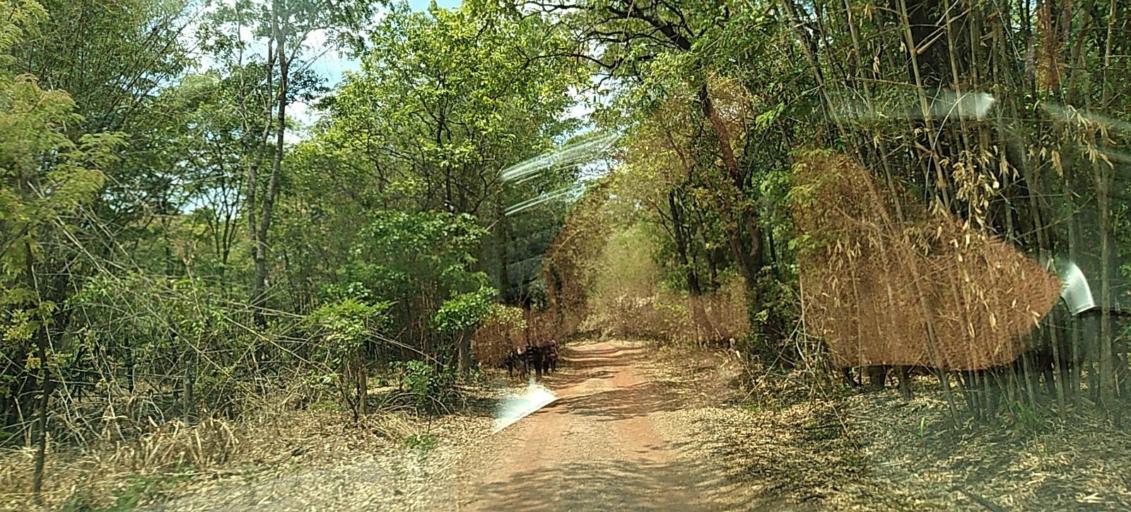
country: ZM
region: Copperbelt
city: Chililabombwe
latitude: -12.4782
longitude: 27.6457
